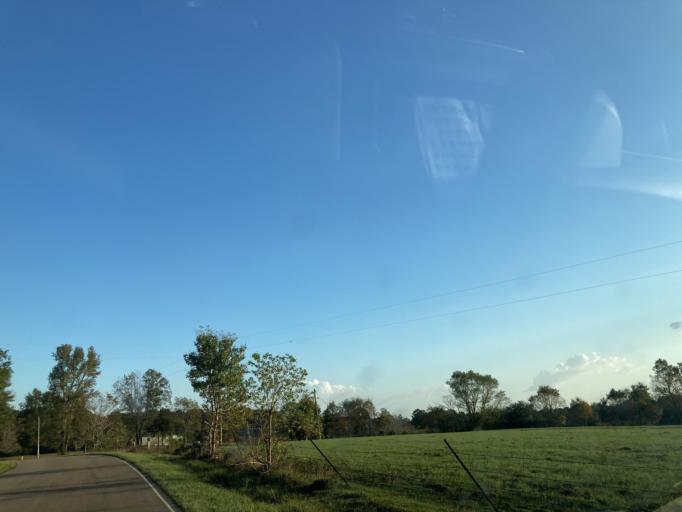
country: US
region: Mississippi
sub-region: Lamar County
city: Sumrall
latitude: 31.4001
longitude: -89.6139
